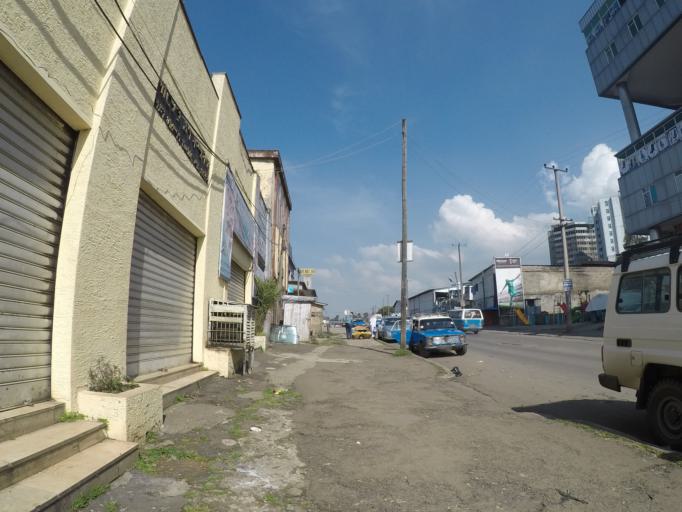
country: ET
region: Adis Abeba
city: Addis Ababa
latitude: 9.0218
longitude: 38.7419
